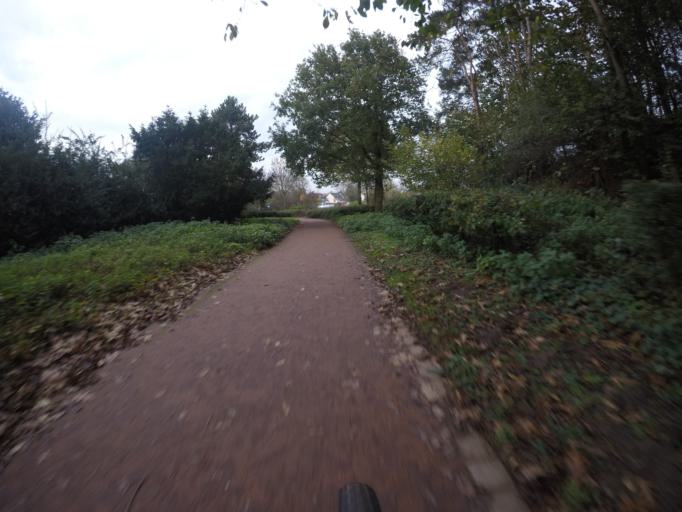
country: DE
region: North Rhine-Westphalia
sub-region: Regierungsbezirk Dusseldorf
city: Bocholt
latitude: 51.8282
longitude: 6.6439
